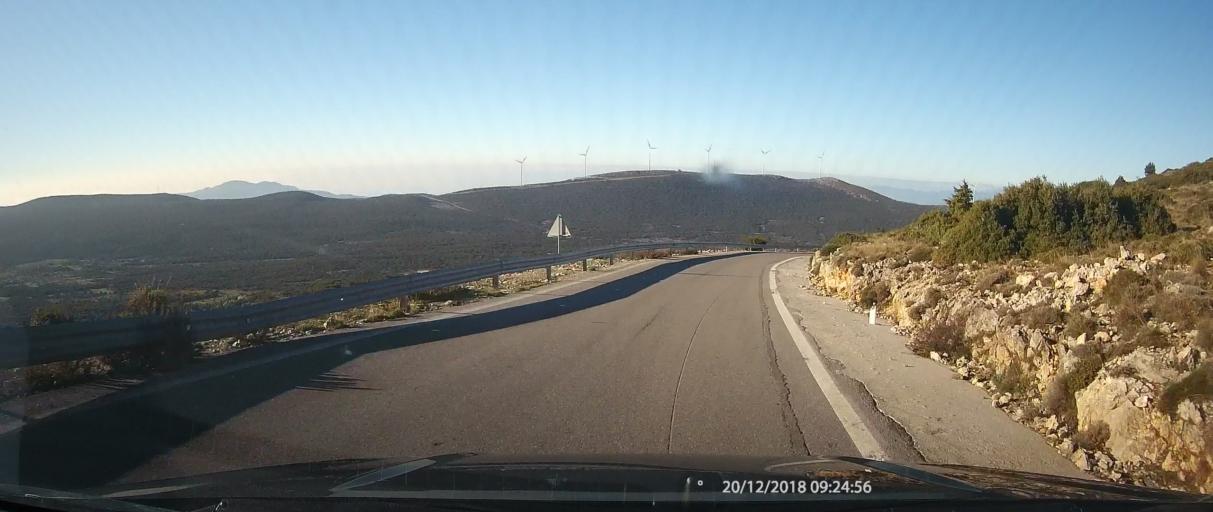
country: GR
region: Peloponnese
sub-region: Nomos Lakonias
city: Molaoi
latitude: 36.9600
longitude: 22.8910
